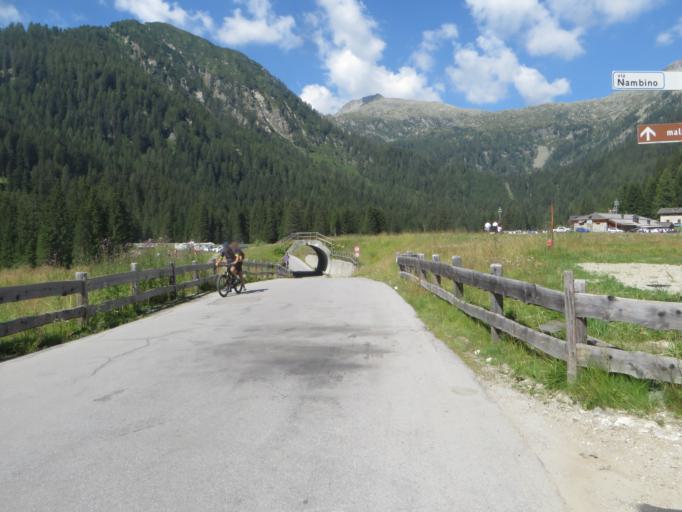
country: IT
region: Trentino-Alto Adige
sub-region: Provincia di Trento
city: Mezzana
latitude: 46.2375
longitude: 10.8193
